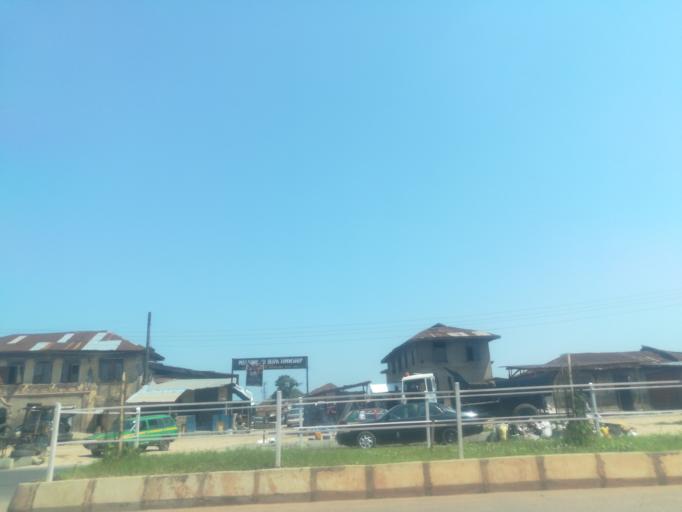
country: NG
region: Ogun
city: Abeokuta
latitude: 7.1678
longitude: 3.3515
